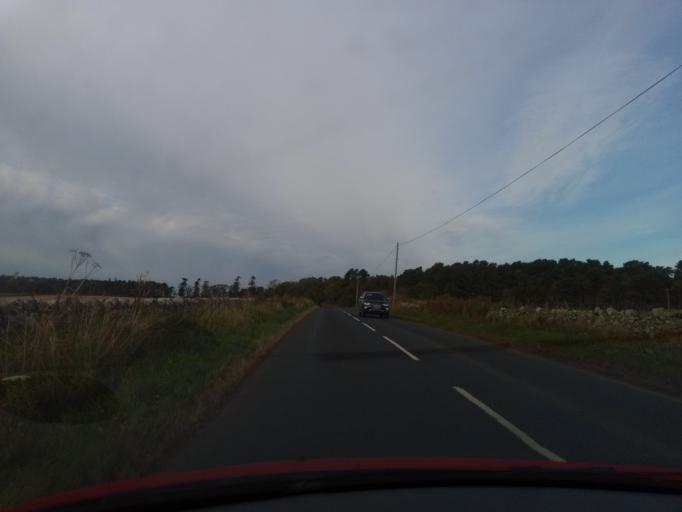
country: GB
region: Scotland
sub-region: The Scottish Borders
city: Kelso
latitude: 55.5644
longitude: -2.3453
